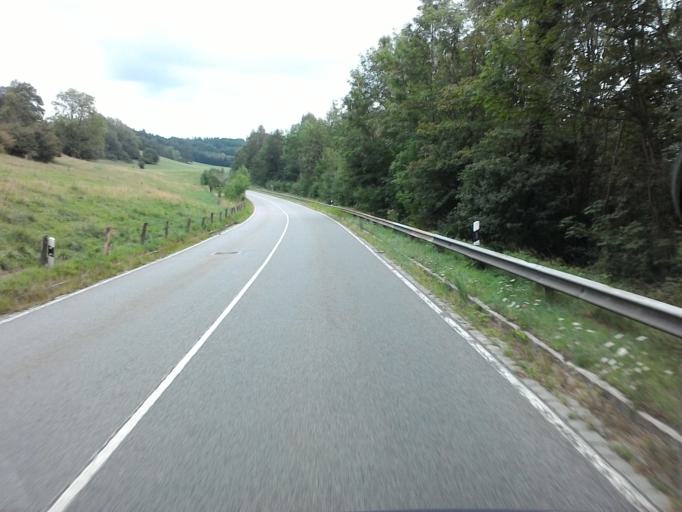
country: DE
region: Bavaria
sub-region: Upper Bavaria
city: Weyarn
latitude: 47.8431
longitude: 11.8124
